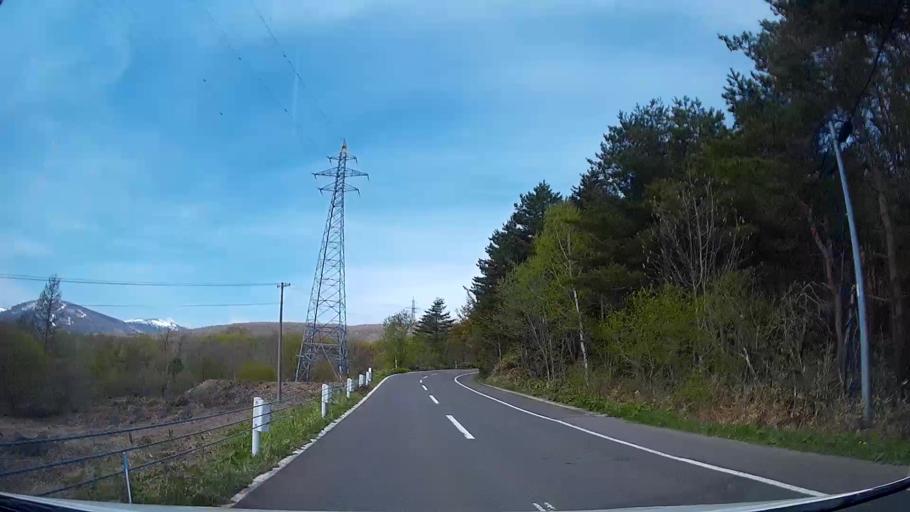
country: JP
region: Iwate
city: Shizukuishi
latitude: 39.9237
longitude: 140.9692
